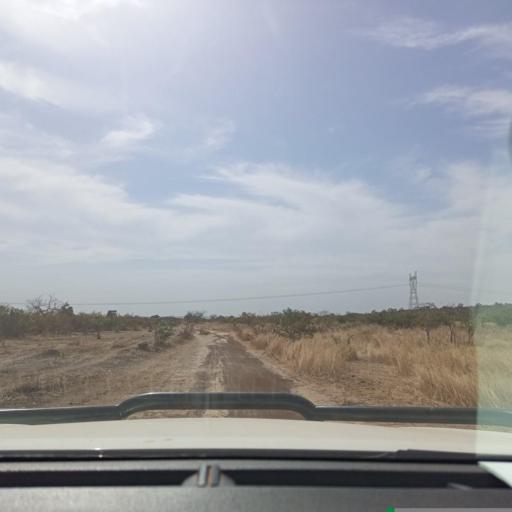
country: ML
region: Koulikoro
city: Kati
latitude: 12.7369
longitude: -8.2505
